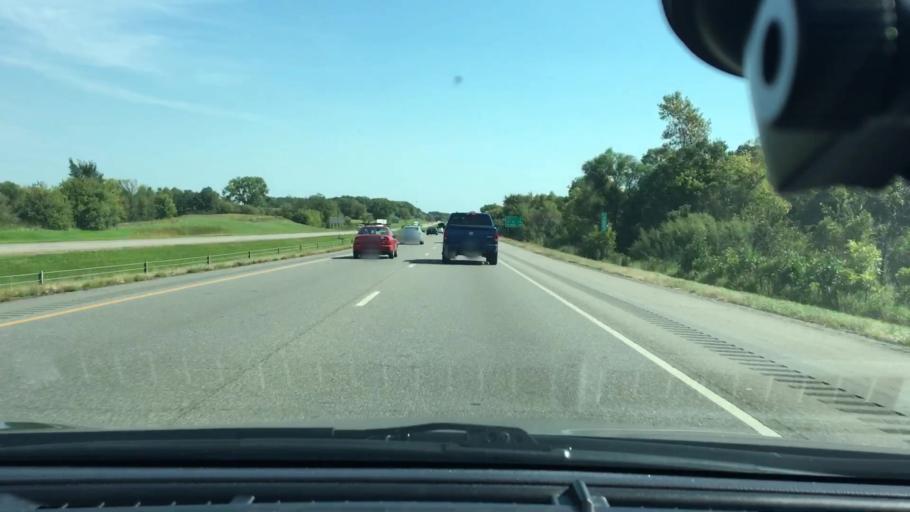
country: US
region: Minnesota
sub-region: Wright County
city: Albertville
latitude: 45.2301
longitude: -93.6327
